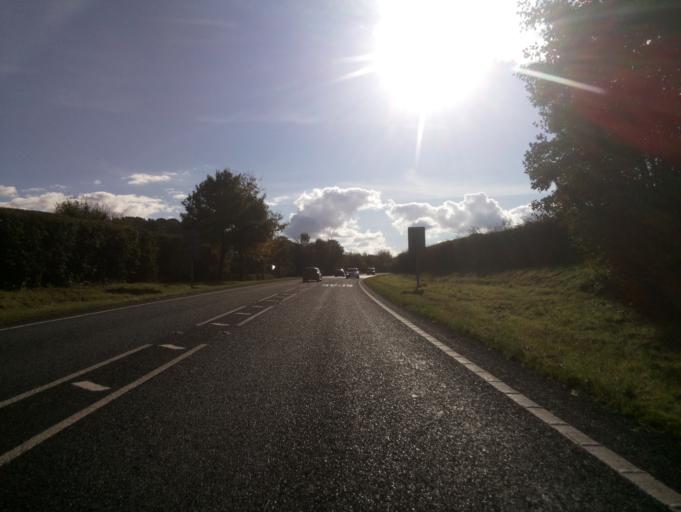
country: GB
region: Wales
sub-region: Sir Powys
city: Brecon
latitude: 51.9776
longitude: -3.3305
